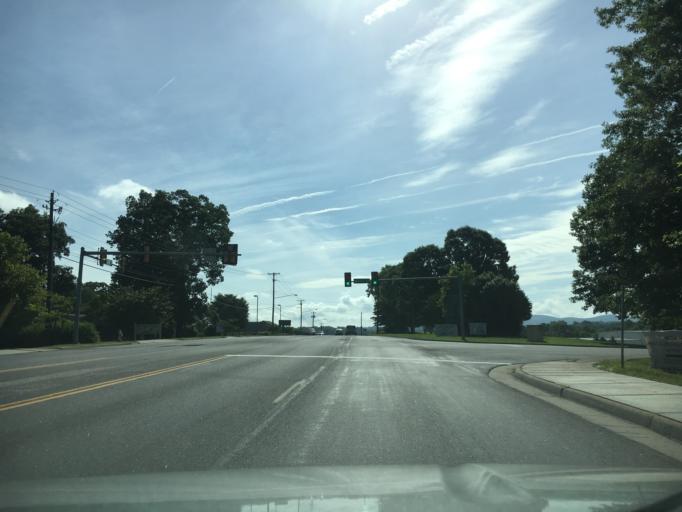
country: US
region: Virginia
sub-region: Bedford County
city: Forest
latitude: 37.3769
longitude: -79.2406
